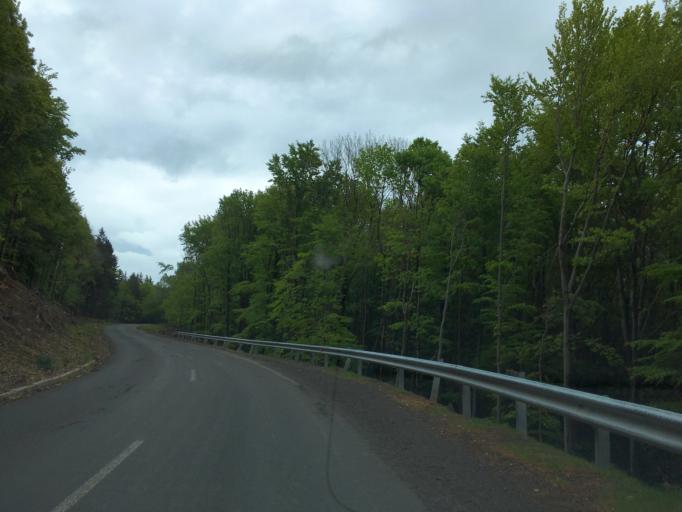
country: HU
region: Nograd
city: Batonyterenye
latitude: 47.9124
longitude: 19.8926
